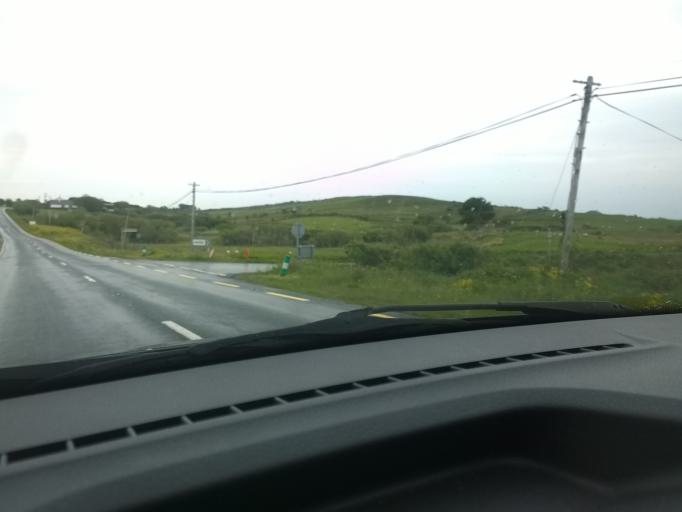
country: IE
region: Connaught
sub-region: Maigh Eo
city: Westport
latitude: 53.9049
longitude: -9.6823
